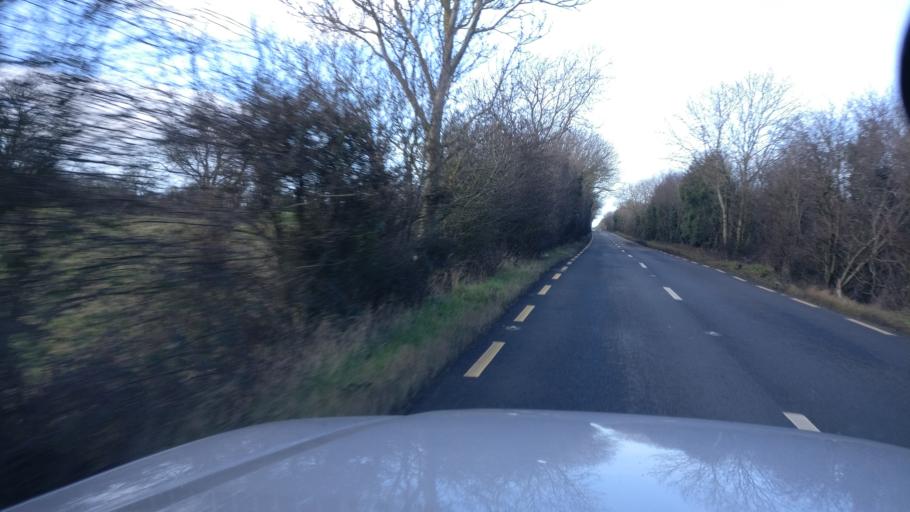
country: IE
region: Leinster
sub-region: Laois
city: Mountmellick
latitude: 53.0783
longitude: -7.3307
